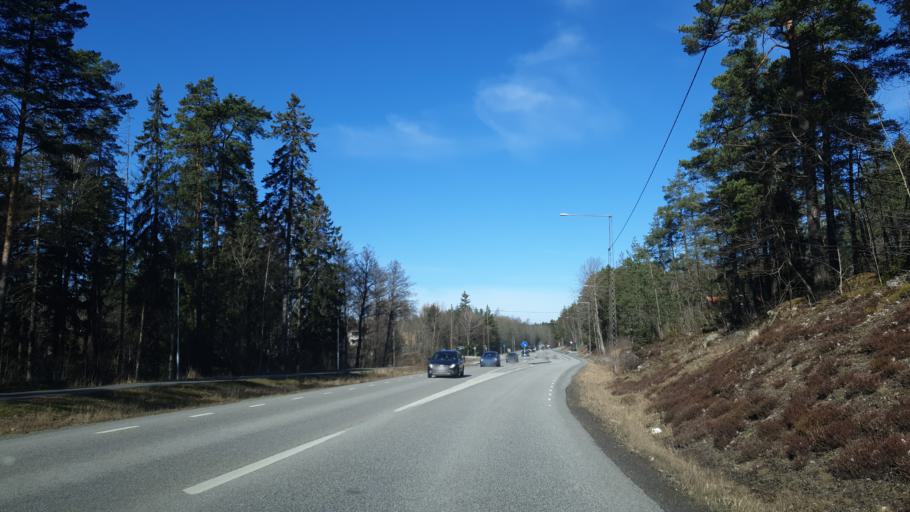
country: SE
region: Stockholm
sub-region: Jarfalla Kommun
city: Jakobsberg
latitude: 59.4387
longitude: 17.8408
